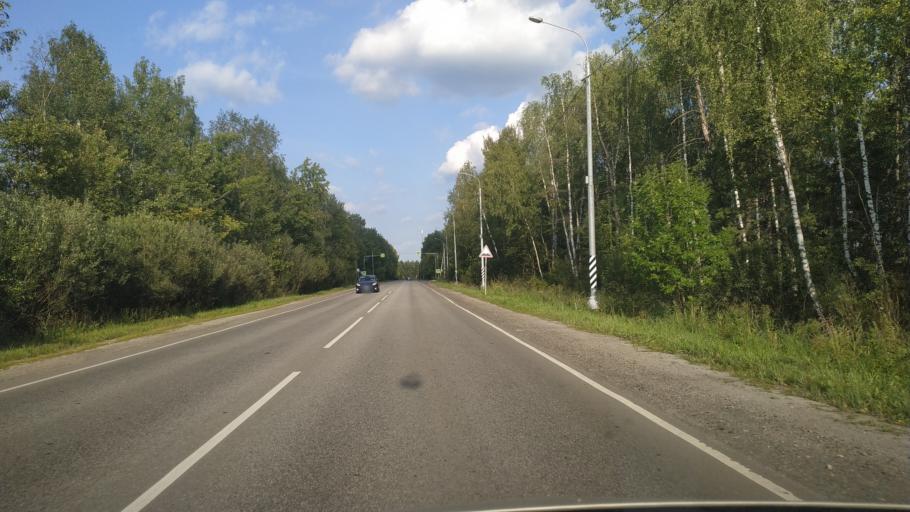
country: RU
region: Moskovskaya
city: Likino-Dulevo
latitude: 55.7285
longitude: 38.9851
